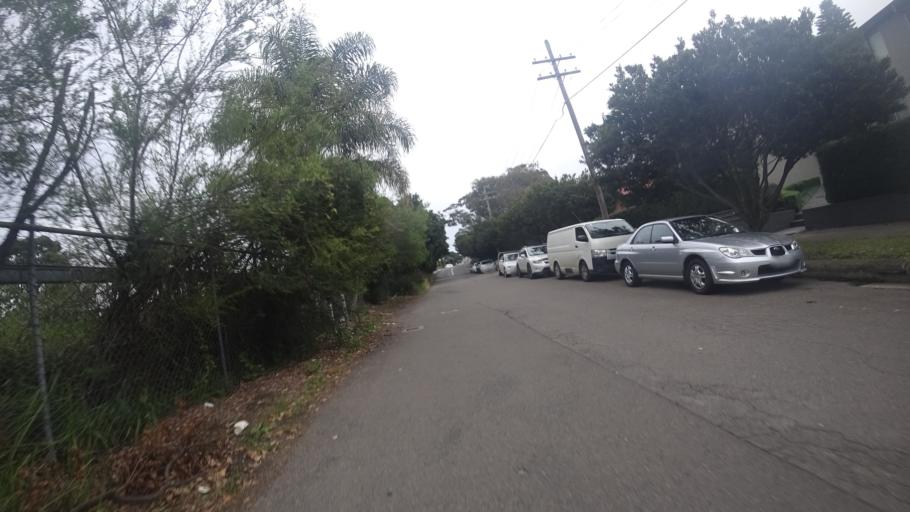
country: AU
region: New South Wales
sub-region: Marrickville
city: Marrickville
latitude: -33.9150
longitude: 151.1589
